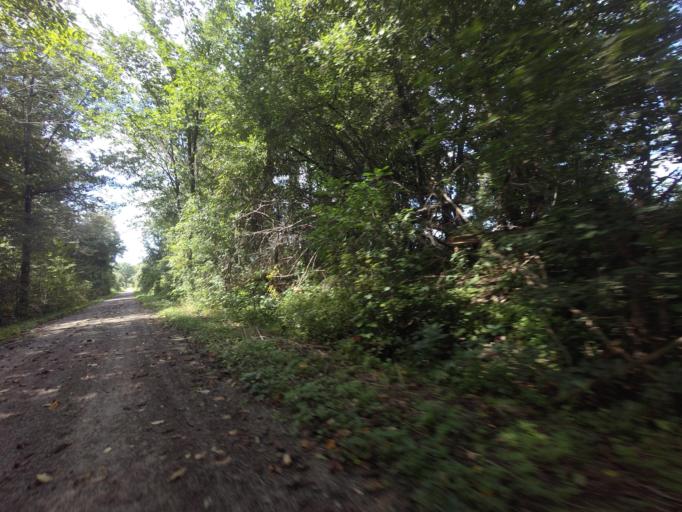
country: CA
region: Ontario
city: Huron East
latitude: 43.6788
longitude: -81.2961
